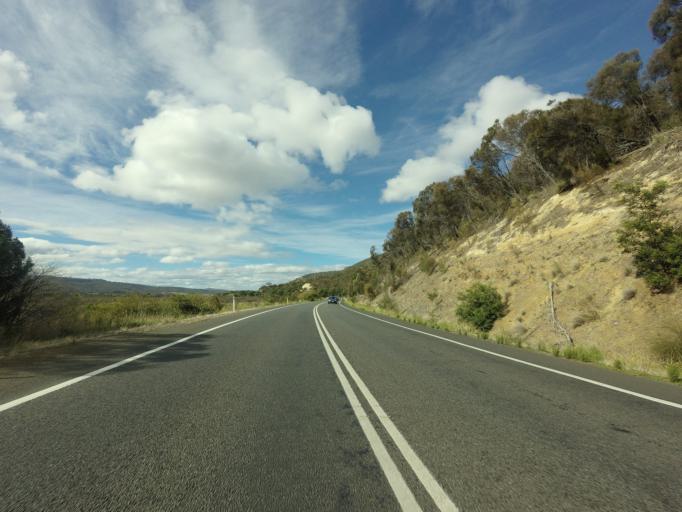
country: AU
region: Tasmania
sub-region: Glenorchy
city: Granton
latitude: -42.7567
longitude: 147.1568
